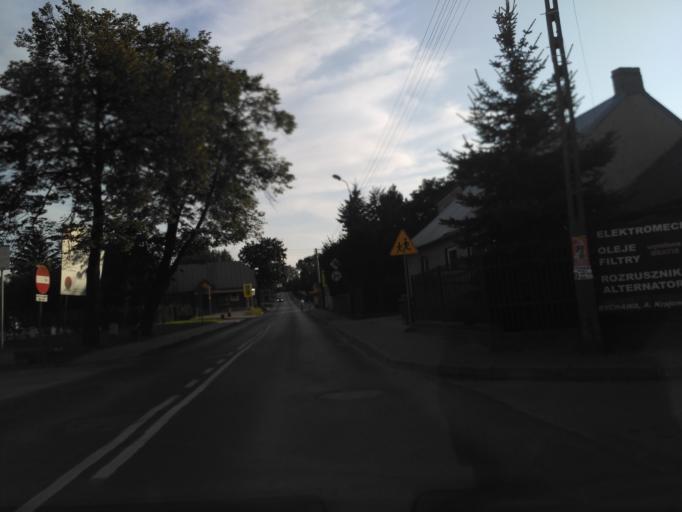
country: PL
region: Lublin Voivodeship
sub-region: Powiat lubelski
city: Bychawa
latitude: 51.0143
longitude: 22.5347
